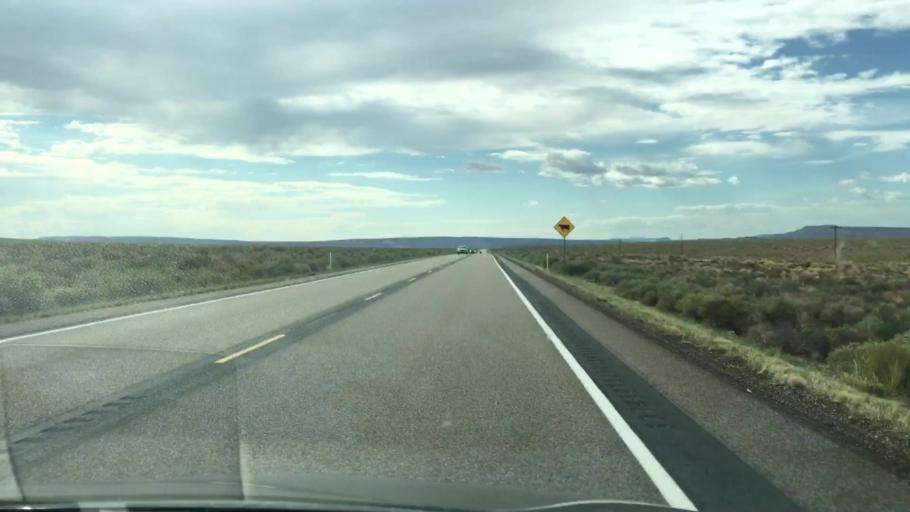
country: US
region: Arizona
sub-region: Coconino County
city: Page
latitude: 37.0935
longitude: -111.7457
